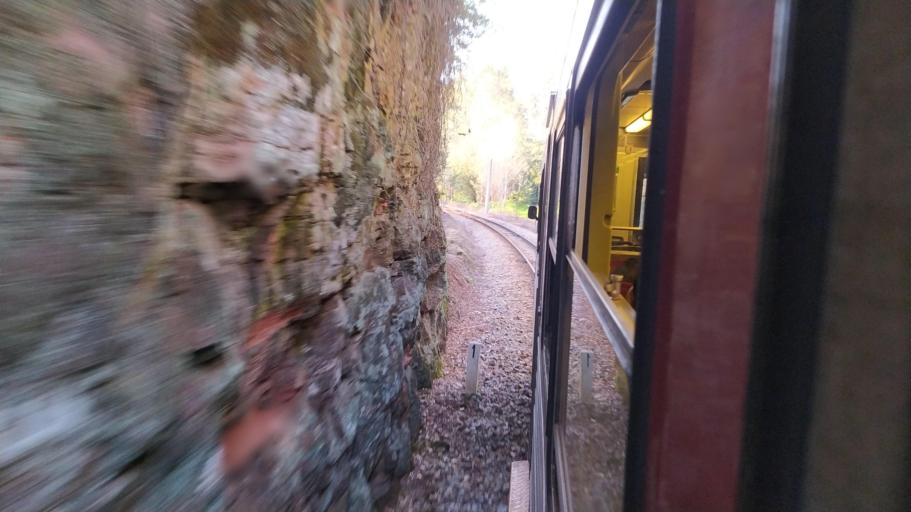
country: PT
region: Aveiro
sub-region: Aveiro
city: Eixo
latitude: 40.6002
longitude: -8.5184
